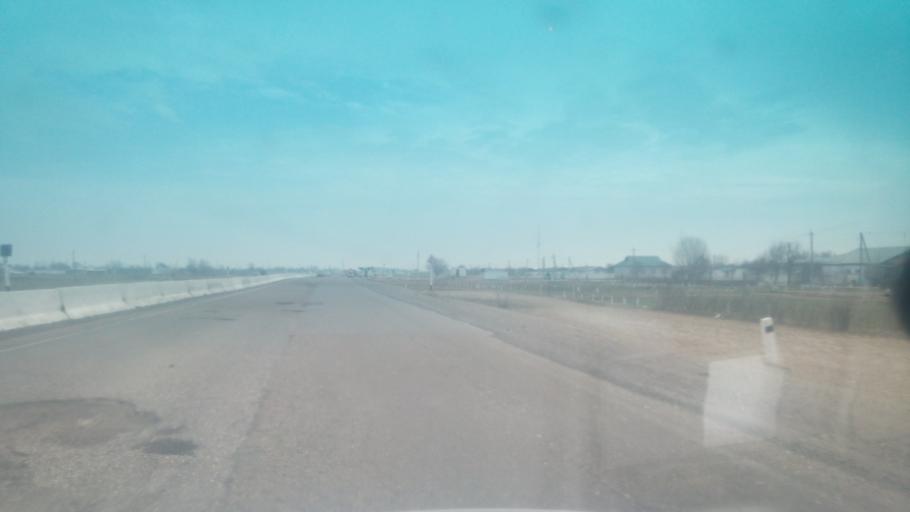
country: KZ
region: Ongtustik Qazaqstan
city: Myrzakent
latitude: 40.5071
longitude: 68.5099
